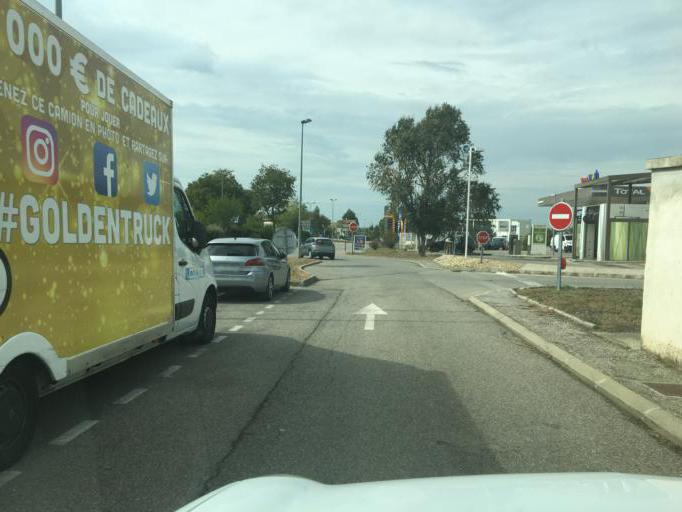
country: FR
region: Provence-Alpes-Cote d'Azur
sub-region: Departement des Bouches-du-Rhone
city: Cabries
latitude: 43.4832
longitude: 5.3840
